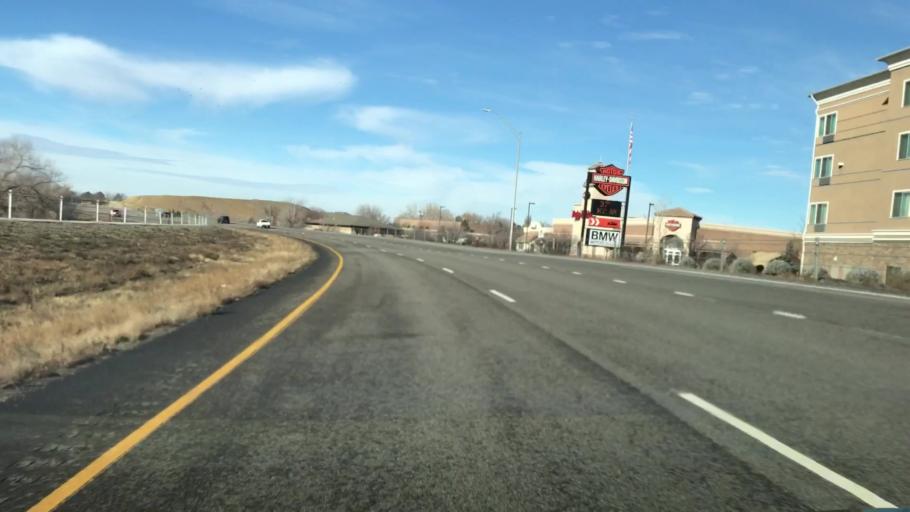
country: US
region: Colorado
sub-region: Mesa County
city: Grand Junction
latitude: 39.1149
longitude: -108.5426
